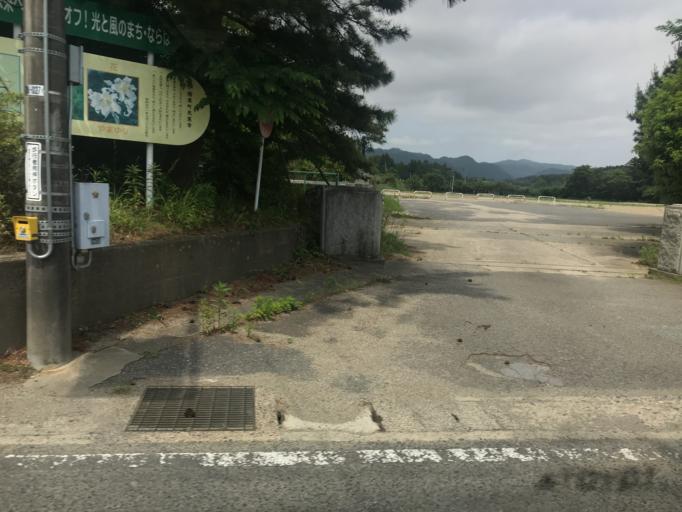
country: JP
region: Fukushima
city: Namie
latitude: 37.2847
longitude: 141.0014
